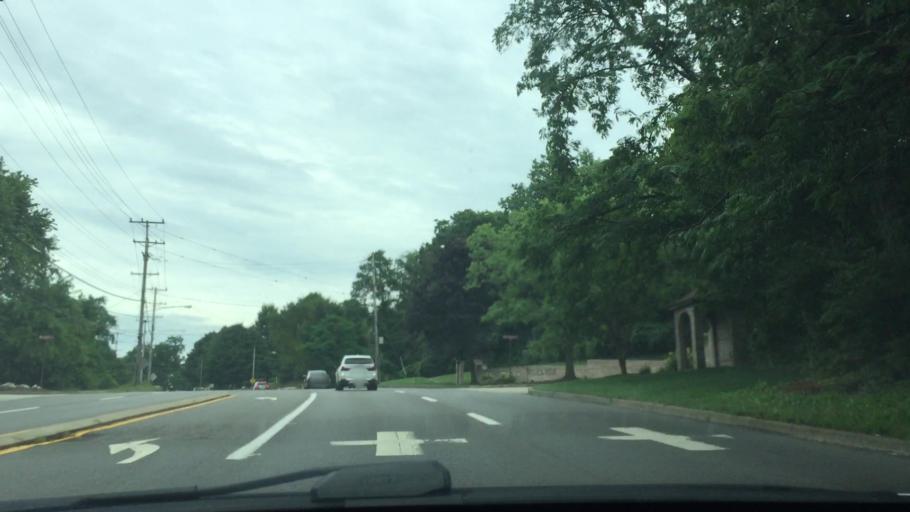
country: US
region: Pennsylvania
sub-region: Allegheny County
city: Mount Lebanon
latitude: 40.3553
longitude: -80.0395
